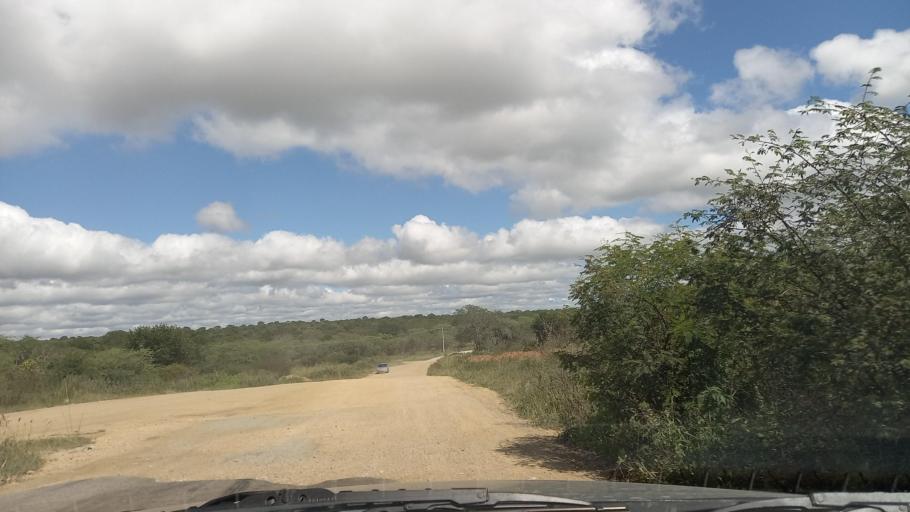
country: BR
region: Pernambuco
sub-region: Caruaru
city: Caruaru
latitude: -8.2238
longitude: -35.9865
